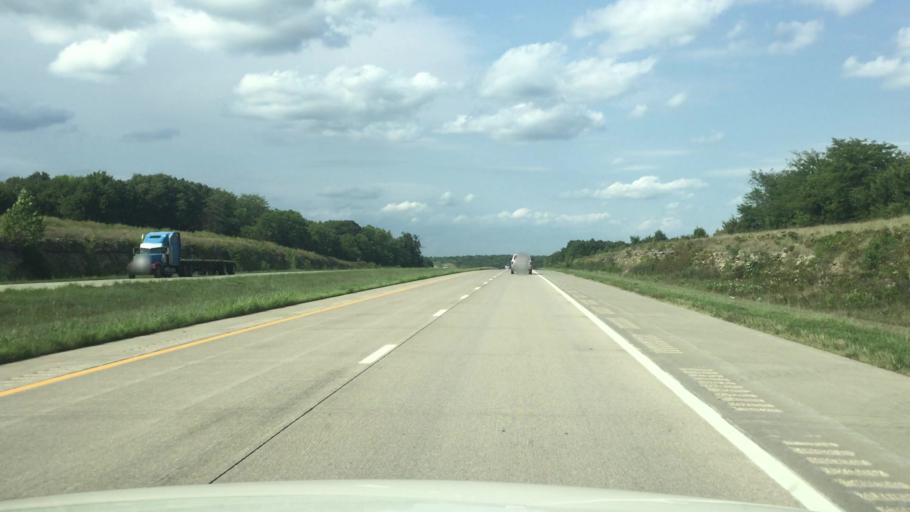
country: US
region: Kansas
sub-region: Miami County
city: Louisburg
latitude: 38.5835
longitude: -94.6948
